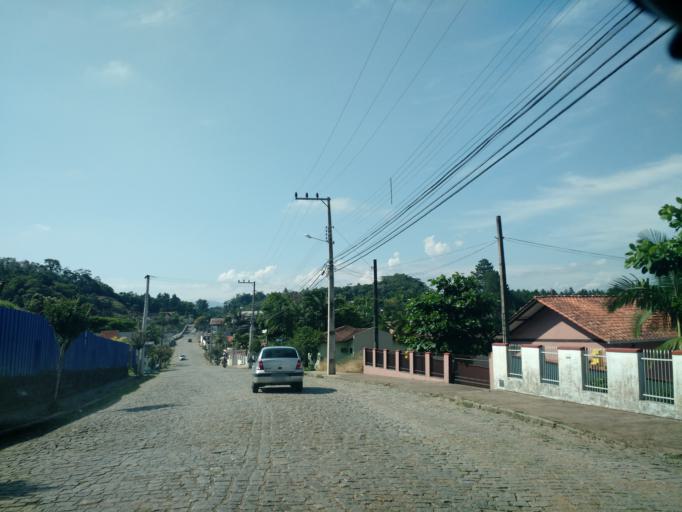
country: BR
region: Santa Catarina
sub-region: Jaragua Do Sul
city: Jaragua do Sul
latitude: -26.5000
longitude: -49.0974
